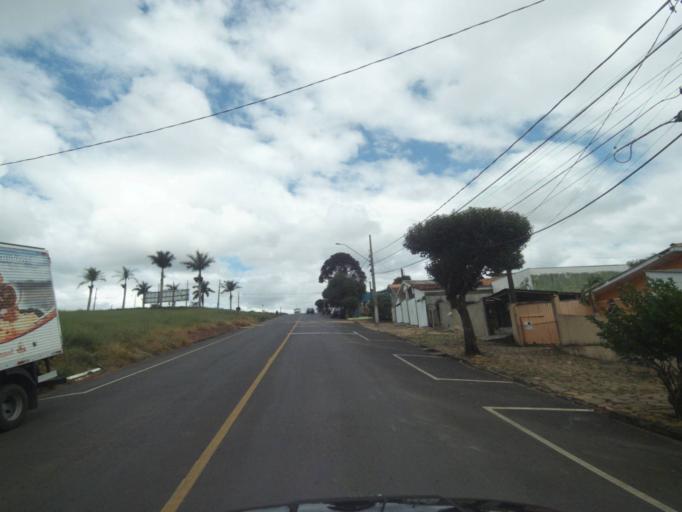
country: BR
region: Parana
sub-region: Telemaco Borba
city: Telemaco Borba
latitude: -24.3172
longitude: -50.6426
